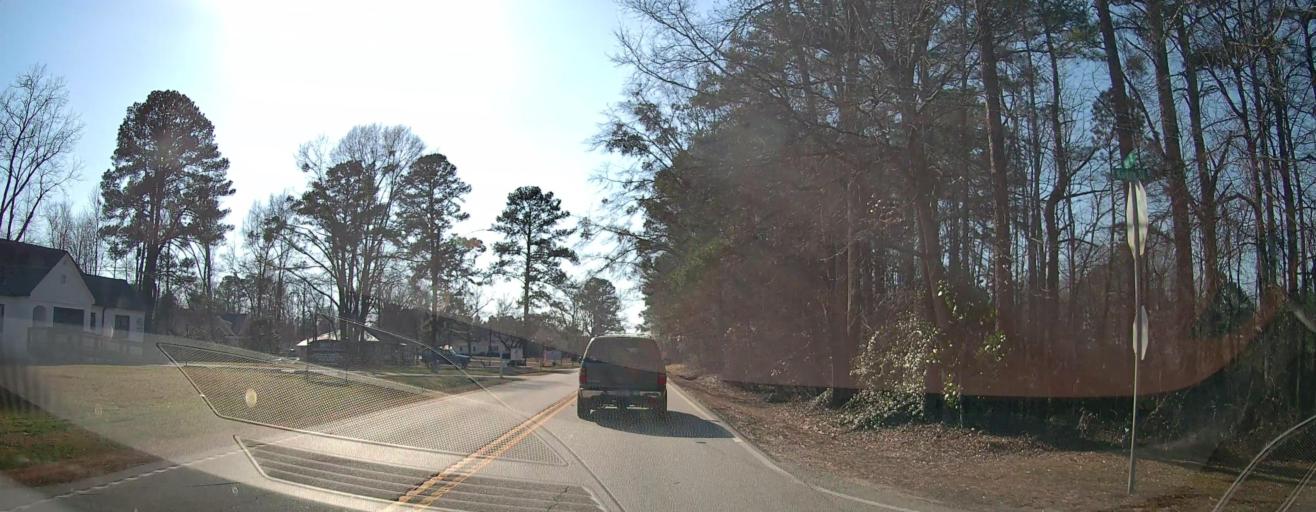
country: US
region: Georgia
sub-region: Henry County
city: Locust Grove
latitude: 33.3234
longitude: -84.0382
